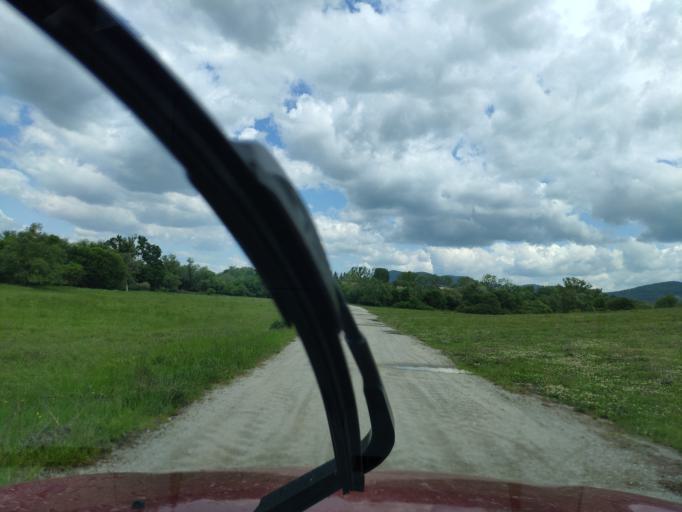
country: SK
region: Kosicky
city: Kosice
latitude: 48.8398
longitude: 21.3205
